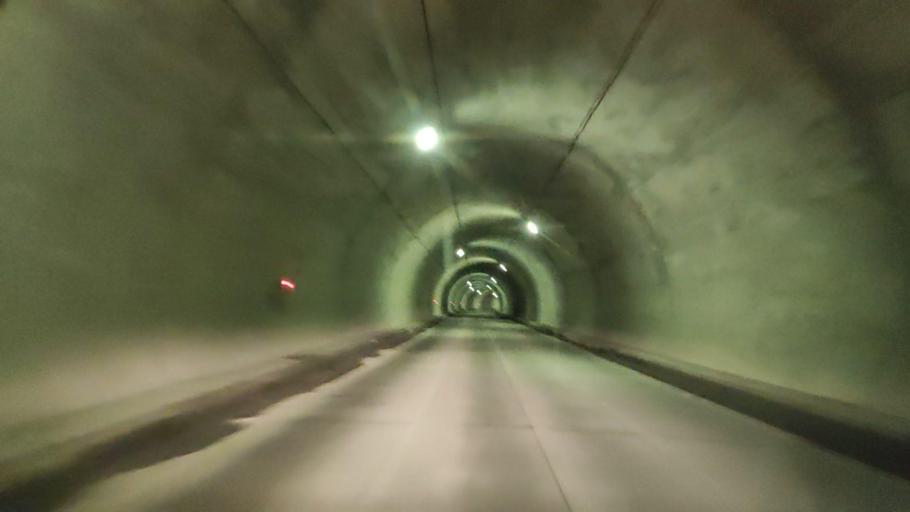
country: JP
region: Fukushima
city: Kitakata
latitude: 37.6830
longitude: 139.7212
